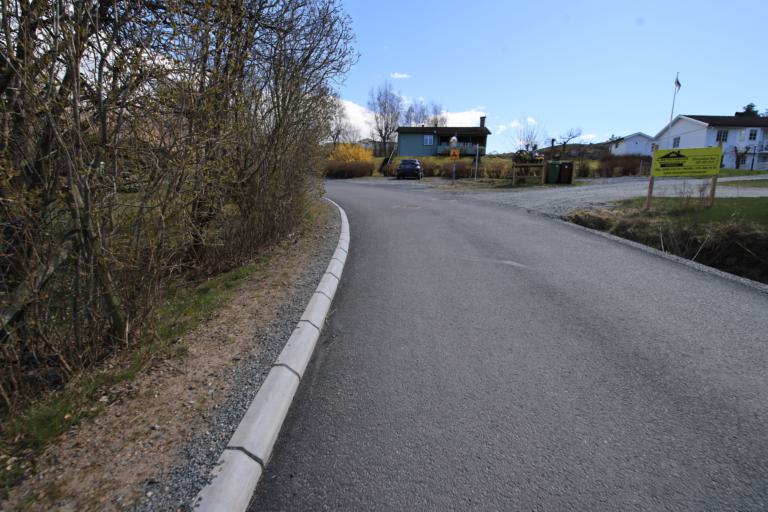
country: SE
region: Halland
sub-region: Varbergs Kommun
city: Varberg
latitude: 57.1807
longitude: 12.2404
